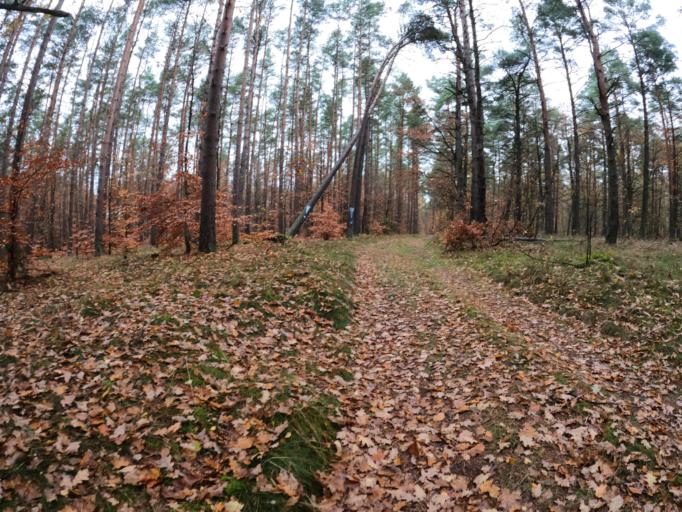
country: PL
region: West Pomeranian Voivodeship
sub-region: Powiat walecki
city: Tuczno
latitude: 53.2775
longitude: 16.2470
